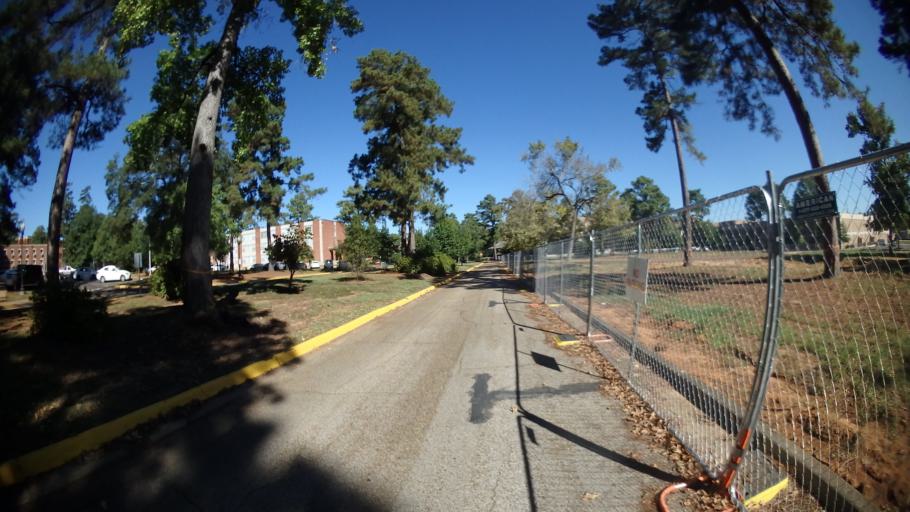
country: US
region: Texas
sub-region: Nacogdoches County
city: Nacogdoches
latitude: 31.6180
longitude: -94.6489
